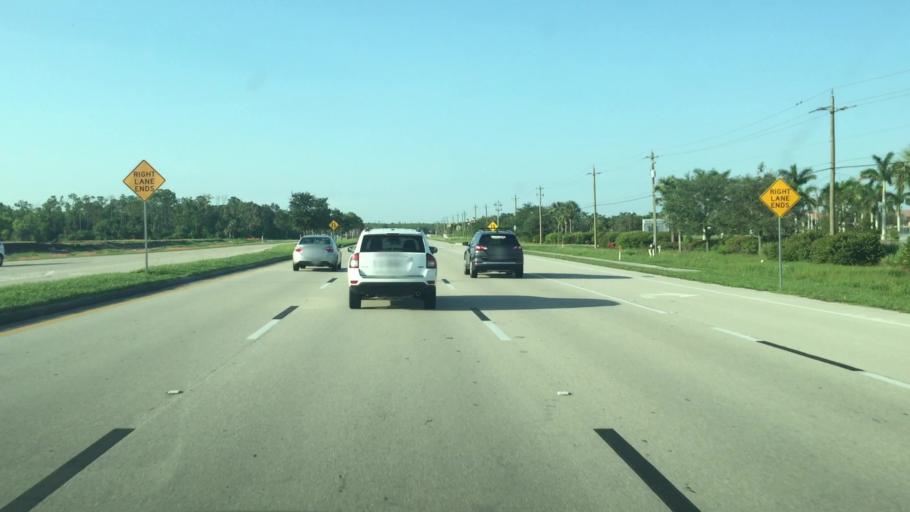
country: US
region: Florida
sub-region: Lee County
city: Fort Myers
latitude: 26.6047
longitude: -81.8113
